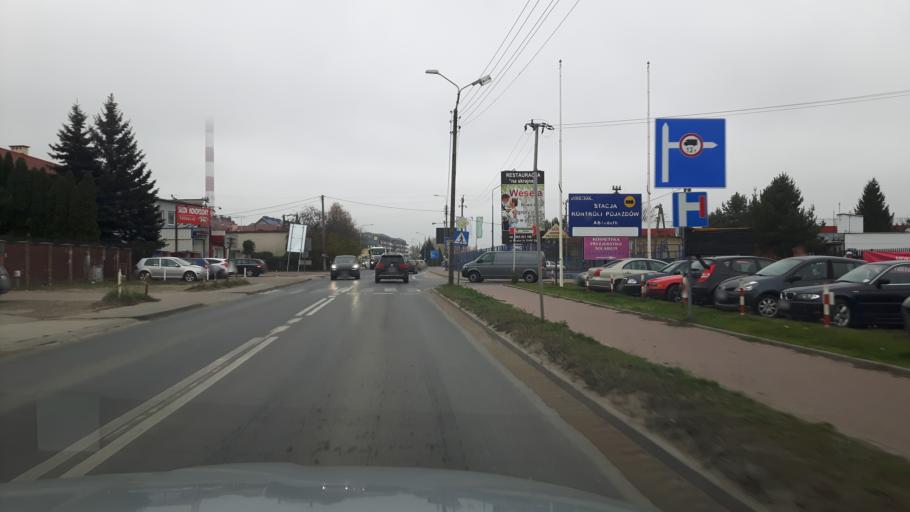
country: PL
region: Masovian Voivodeship
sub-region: Powiat wolominski
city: Zabki
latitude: 52.2791
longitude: 21.1141
